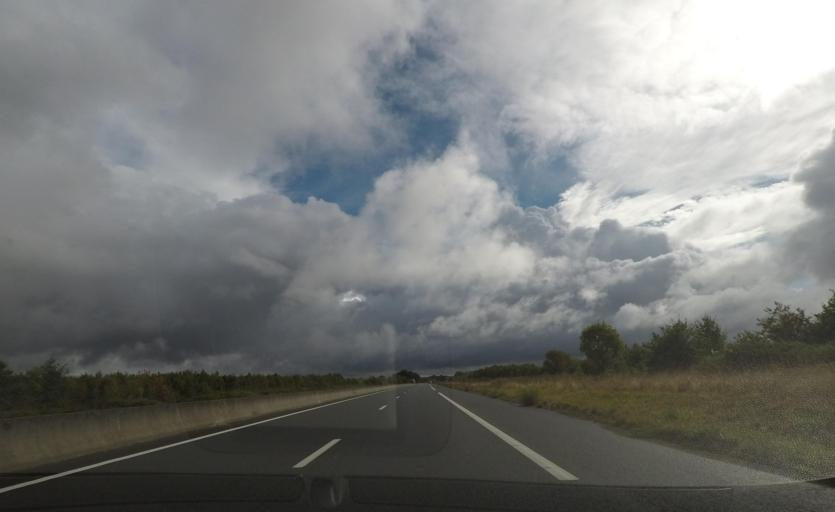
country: FR
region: Pays de la Loire
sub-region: Departement de la Vendee
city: La Roche-sur-Yon
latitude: 46.6606
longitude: -1.3739
